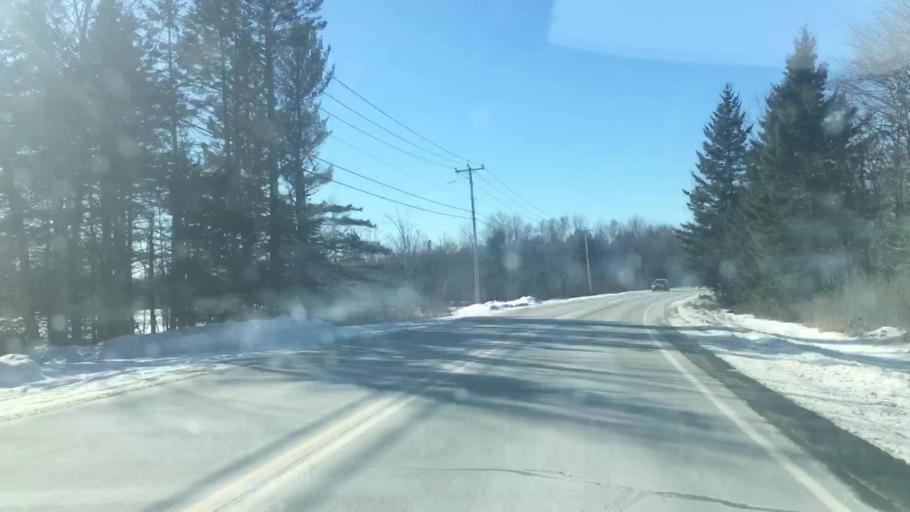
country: US
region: Maine
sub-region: Hancock County
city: Ellsworth
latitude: 44.4952
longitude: -68.4464
